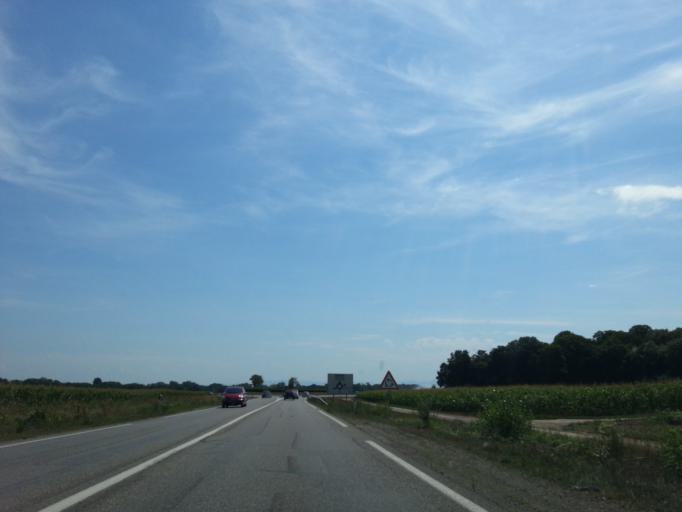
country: FR
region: Alsace
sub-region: Departement du Haut-Rhin
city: Horbourg-Wihr
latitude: 48.0668
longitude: 7.3915
